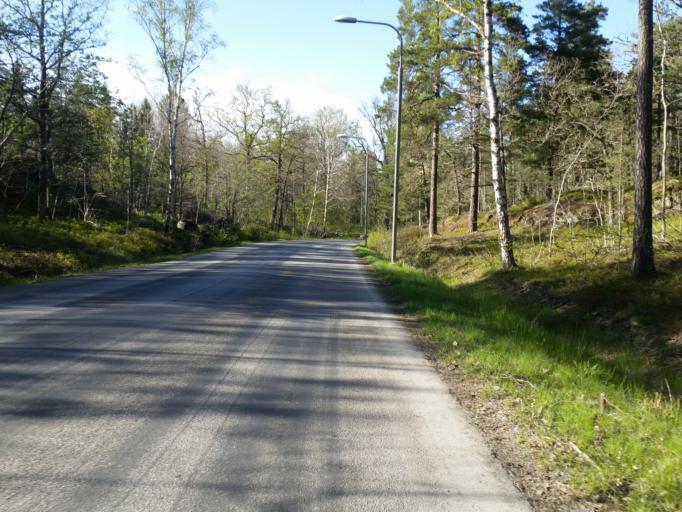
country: SE
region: Stockholm
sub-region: Nacka Kommun
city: Alta
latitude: 59.2550
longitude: 18.1360
